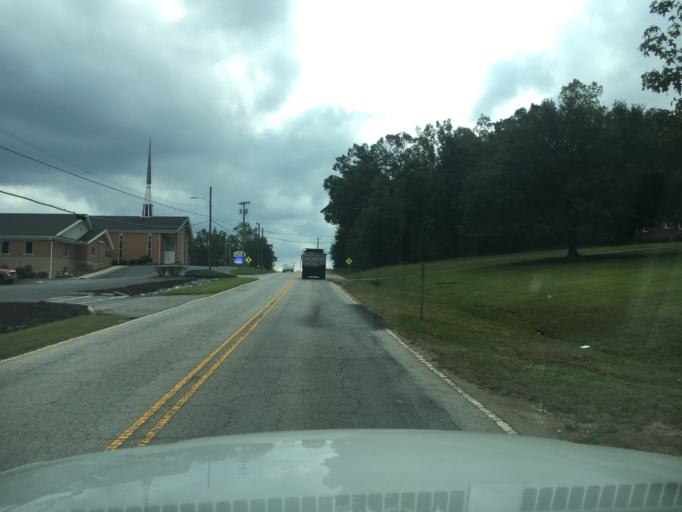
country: US
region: South Carolina
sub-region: Greenville County
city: Greer
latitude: 35.0001
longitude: -82.2515
